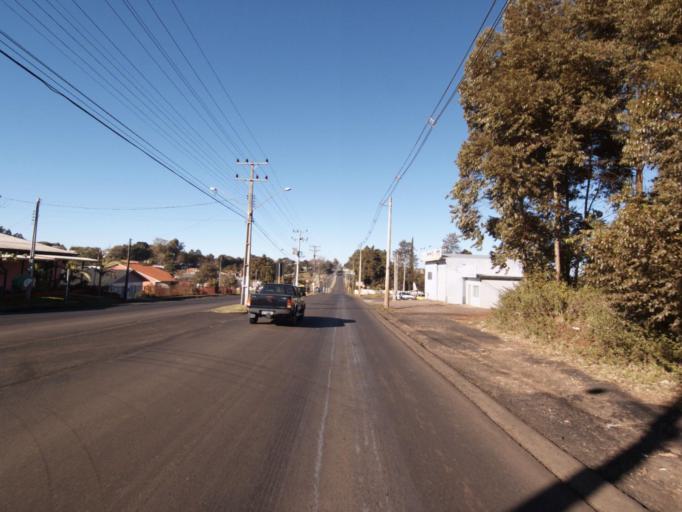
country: AR
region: Misiones
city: Bernardo de Irigoyen
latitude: -26.7394
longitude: -53.5013
